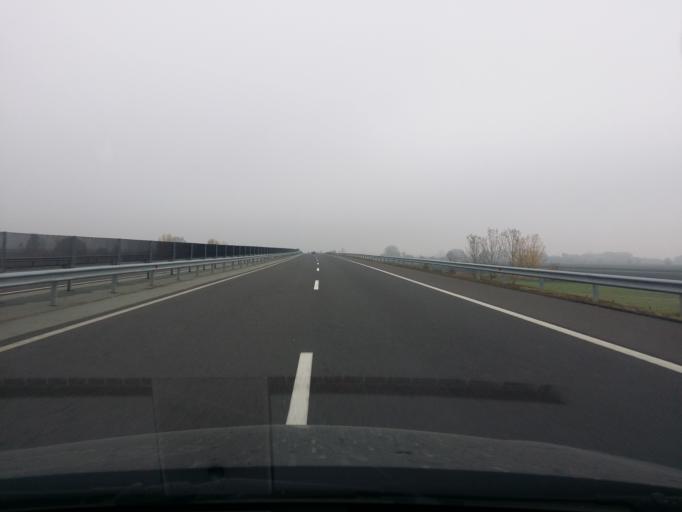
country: HU
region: Hajdu-Bihar
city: Gorbehaza
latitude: 47.8038
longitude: 21.2955
